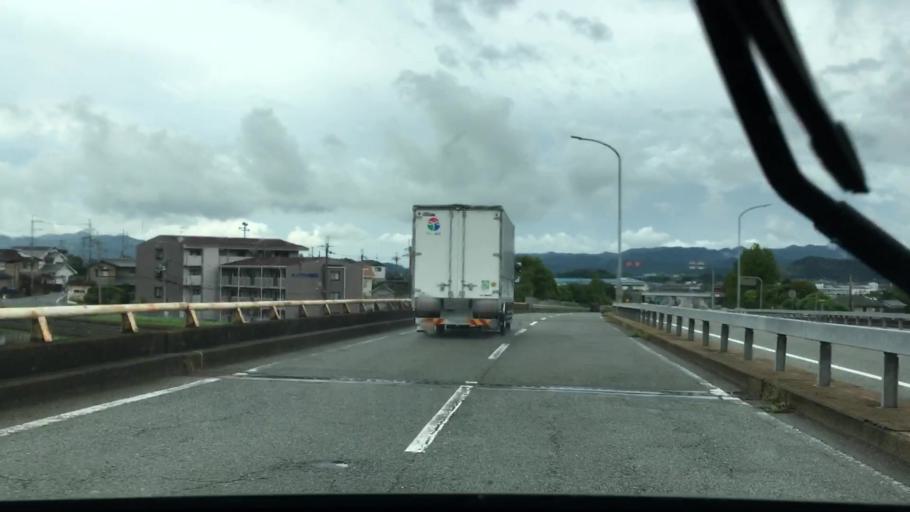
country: JP
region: Hyogo
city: Himeji
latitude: 34.9527
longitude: 134.7693
